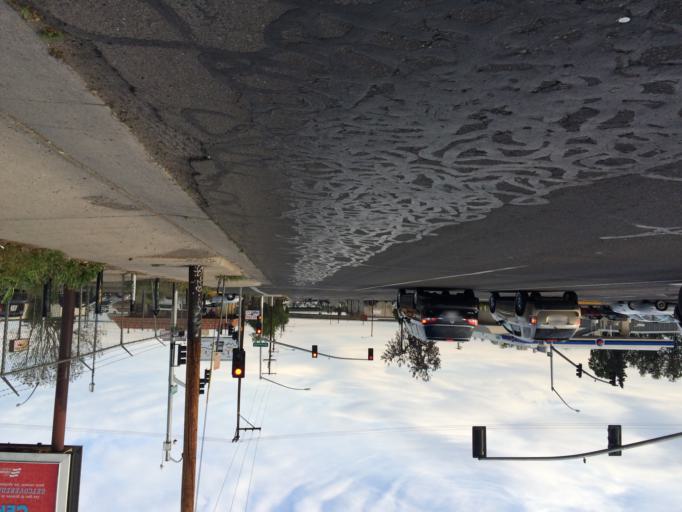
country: US
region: California
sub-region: Fresno County
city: Fresno
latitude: 36.7500
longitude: -119.7454
